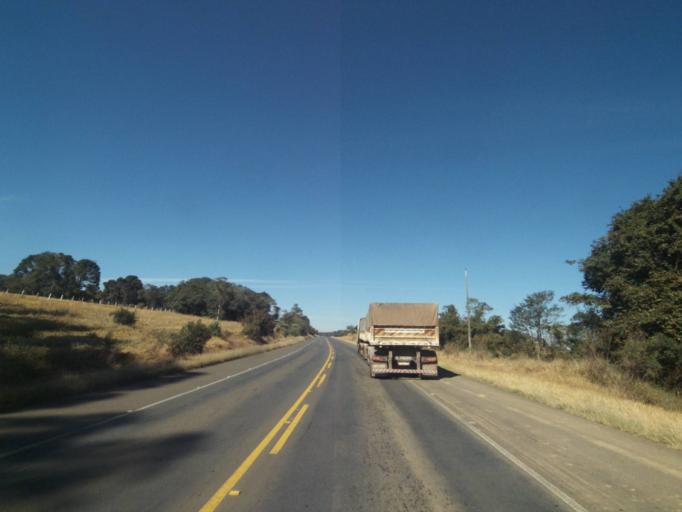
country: BR
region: Parana
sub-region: Tibagi
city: Tibagi
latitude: -24.7634
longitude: -50.4699
